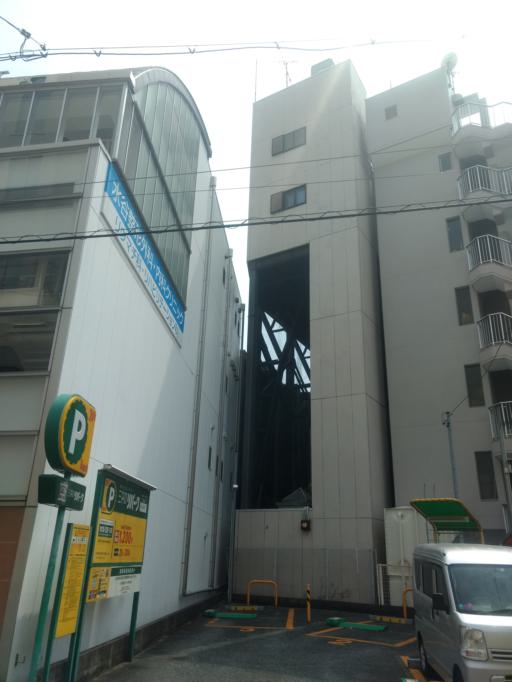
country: JP
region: Aichi
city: Nagoya-shi
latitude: 35.1419
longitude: 136.9001
